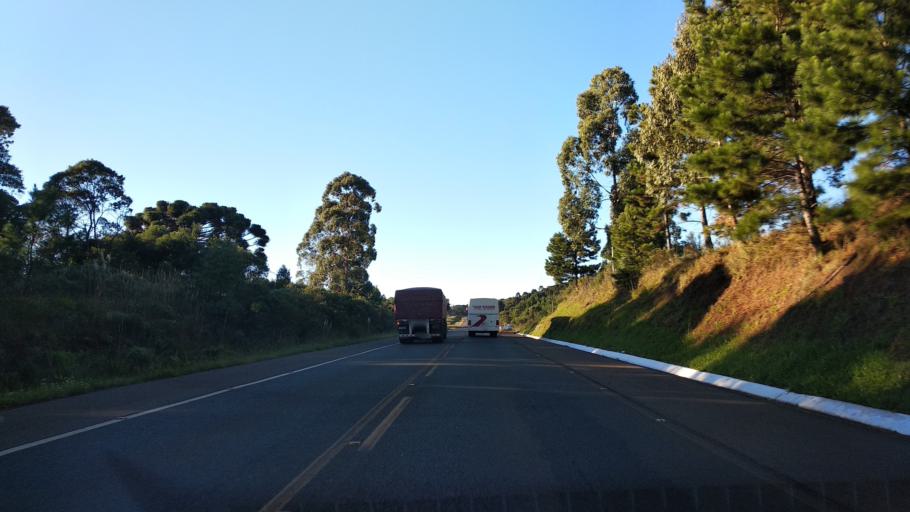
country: BR
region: Santa Catarina
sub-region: Correia Pinto
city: Correia Pinto
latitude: -27.6406
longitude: -50.5967
